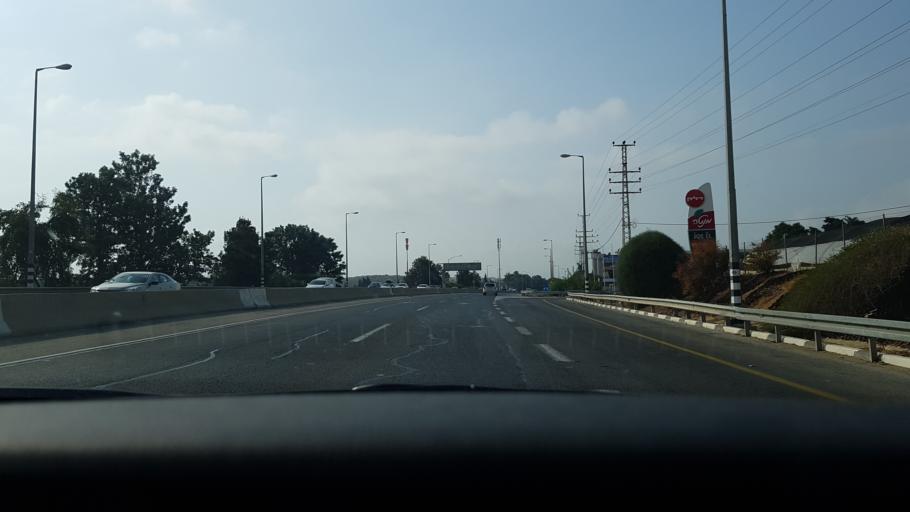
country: IL
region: Central District
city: Ness Ziona
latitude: 31.9386
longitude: 34.7792
